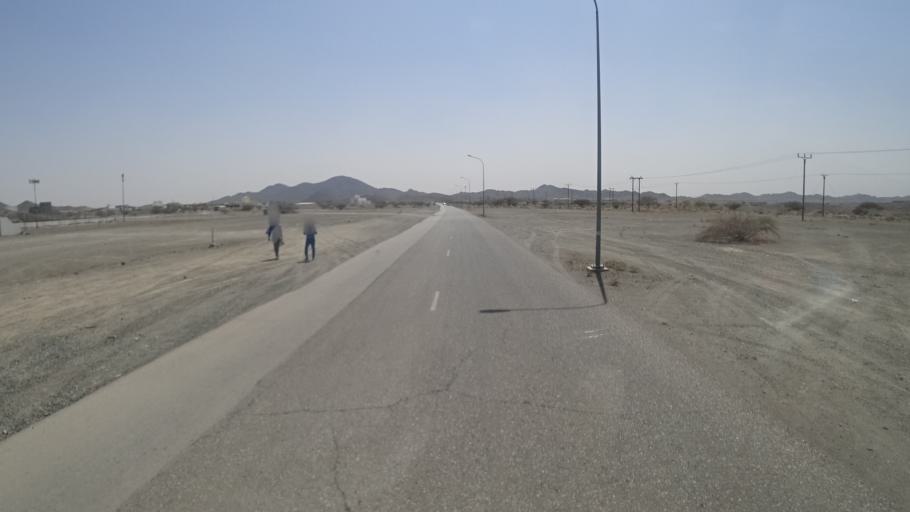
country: OM
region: Ash Sharqiyah
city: Ibra'
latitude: 22.6592
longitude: 58.5261
